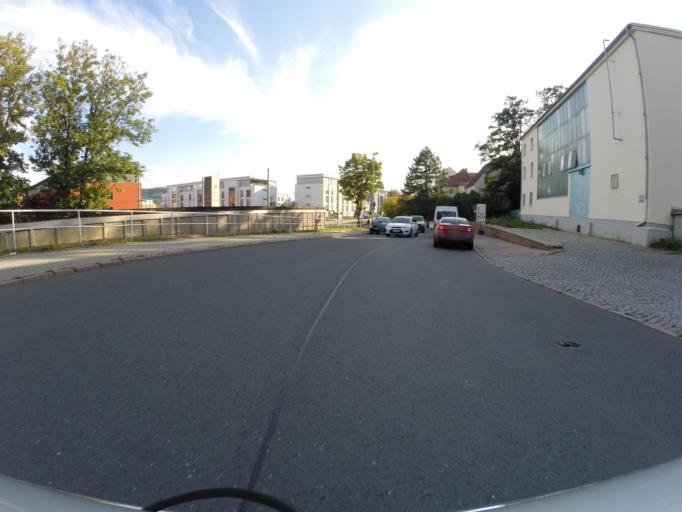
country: DE
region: Thuringia
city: Jena
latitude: 50.9498
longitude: 11.6023
